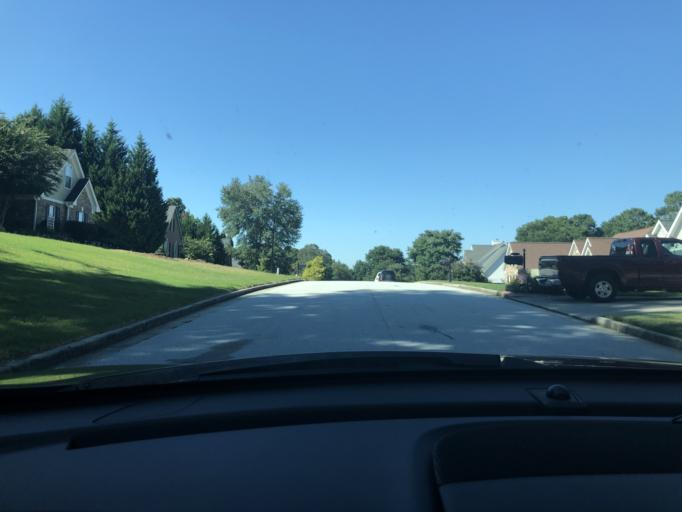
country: US
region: Georgia
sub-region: Gwinnett County
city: Grayson
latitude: 33.9086
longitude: -83.9213
